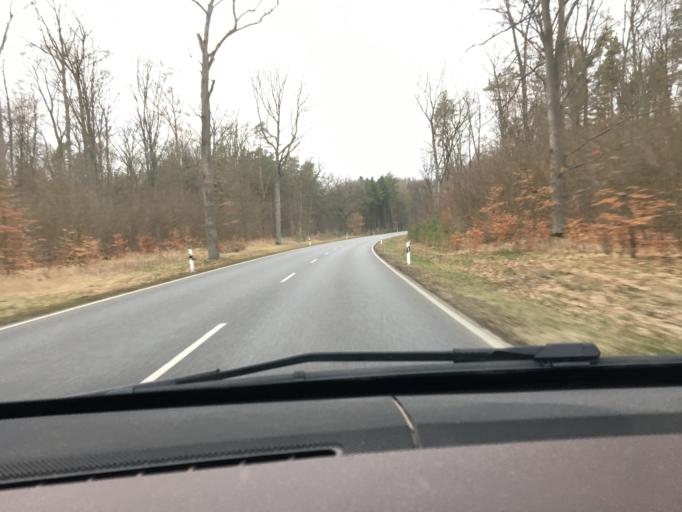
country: DE
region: Brandenburg
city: Liebenwalde
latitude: 52.8708
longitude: 13.4931
